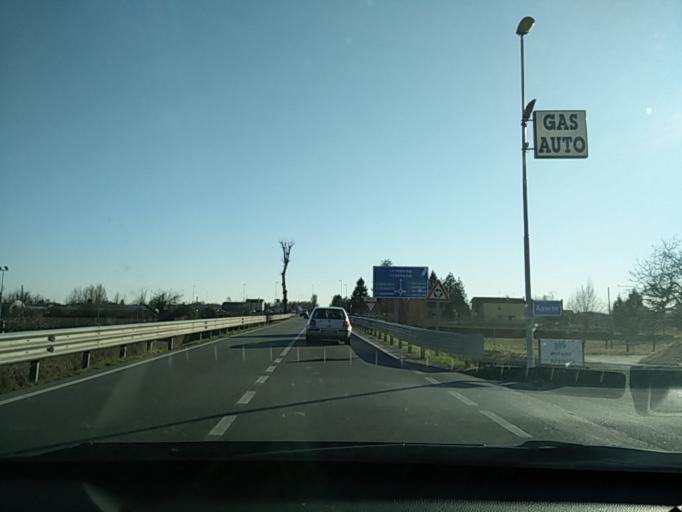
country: IT
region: Veneto
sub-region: Provincia di Treviso
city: Oderzo
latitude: 45.7628
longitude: 12.4852
